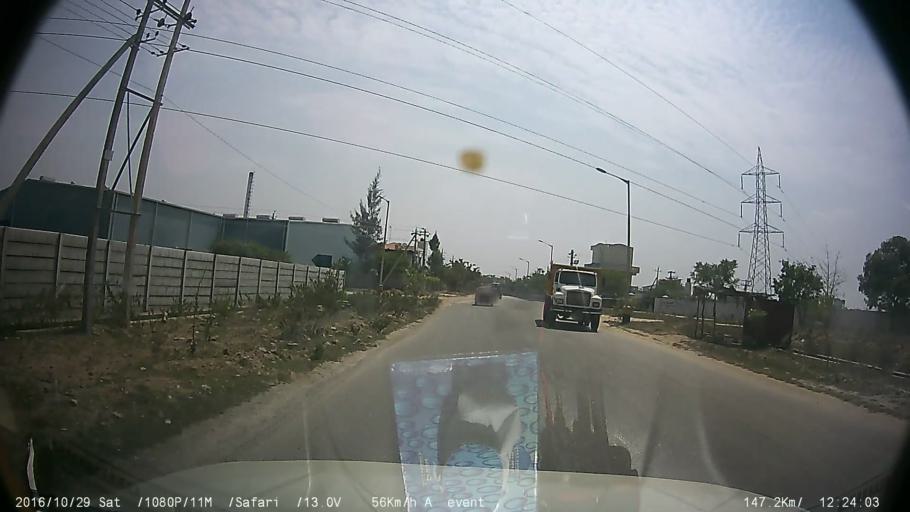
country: IN
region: Karnataka
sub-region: Mysore
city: Mysore
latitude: 12.3558
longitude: 76.5639
